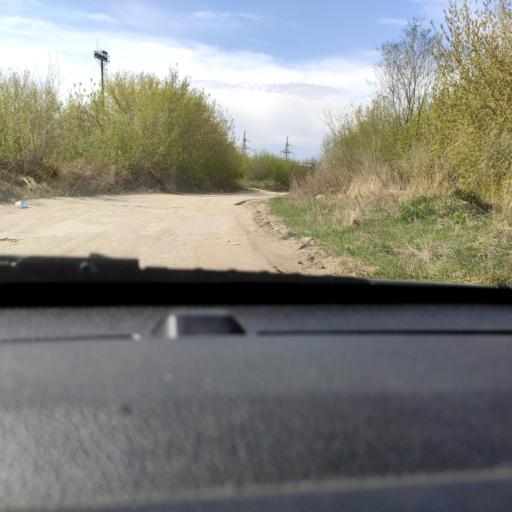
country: RU
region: Samara
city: Podstepki
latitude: 53.5761
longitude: 49.2301
